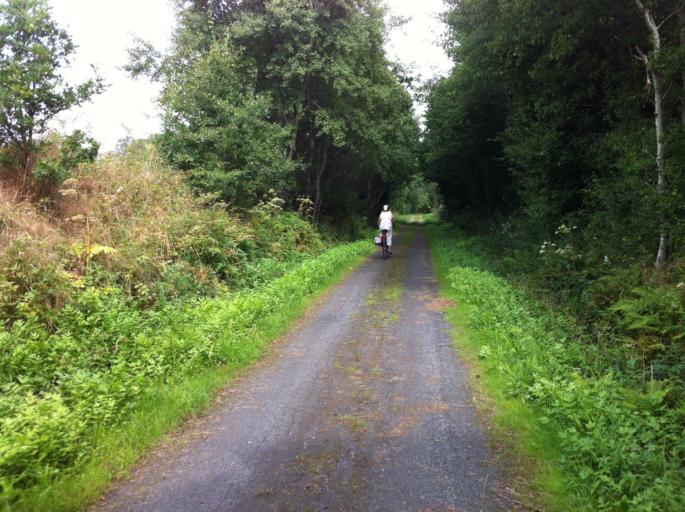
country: SE
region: Skane
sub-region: Hassleholms Kommun
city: Vinslov
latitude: 55.9388
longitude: 13.8269
